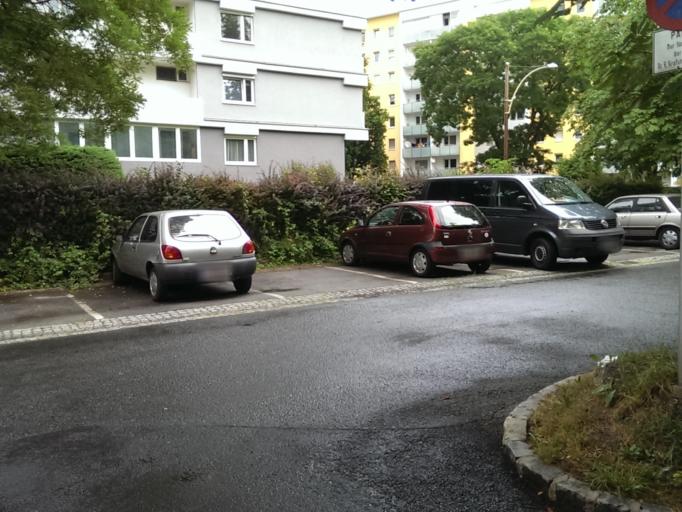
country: AT
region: Styria
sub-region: Graz Stadt
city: Graz
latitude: 47.0646
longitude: 15.4696
